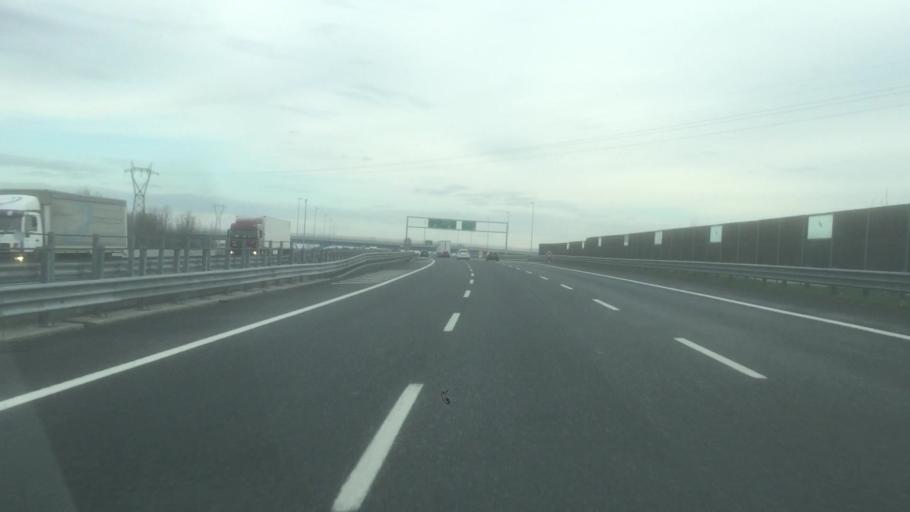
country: IT
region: Veneto
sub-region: Provincia di Venezia
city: Martellago
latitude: 45.5544
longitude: 12.1492
